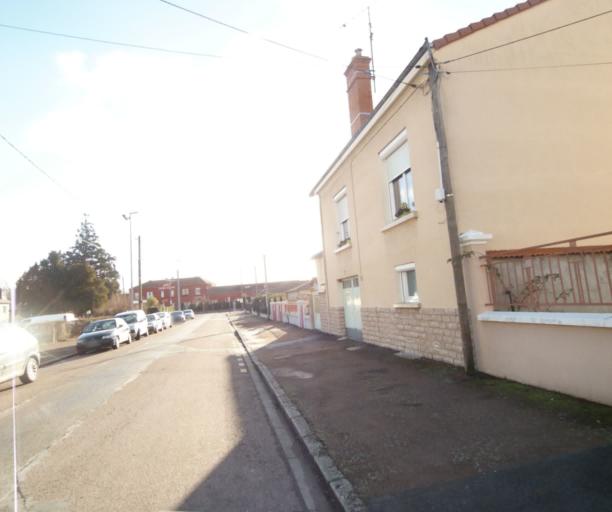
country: FR
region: Rhone-Alpes
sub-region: Departement de la Loire
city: Roanne
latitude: 46.0491
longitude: 4.0820
